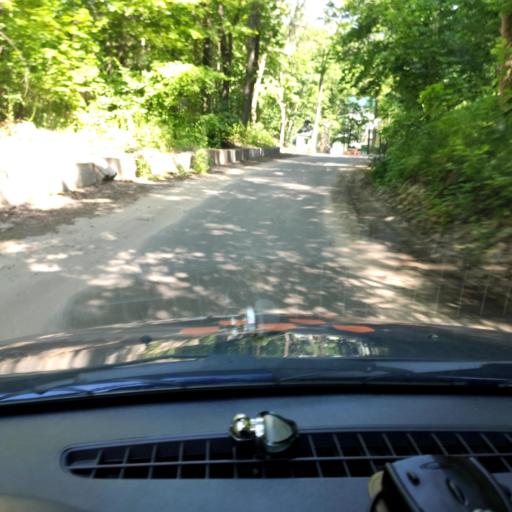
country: RU
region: Voronezj
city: Ramon'
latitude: 51.8297
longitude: 39.2760
